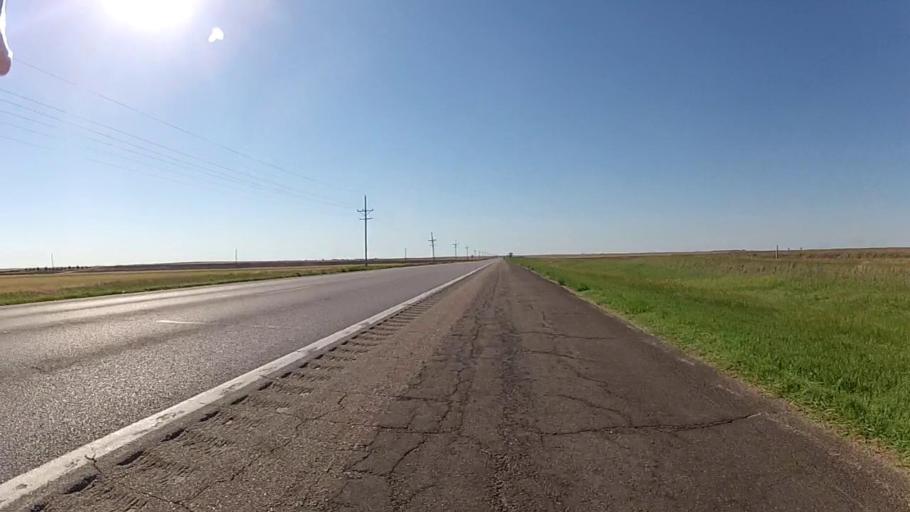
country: US
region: Kansas
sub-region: Ford County
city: Dodge City
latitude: 37.6043
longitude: -99.7060
